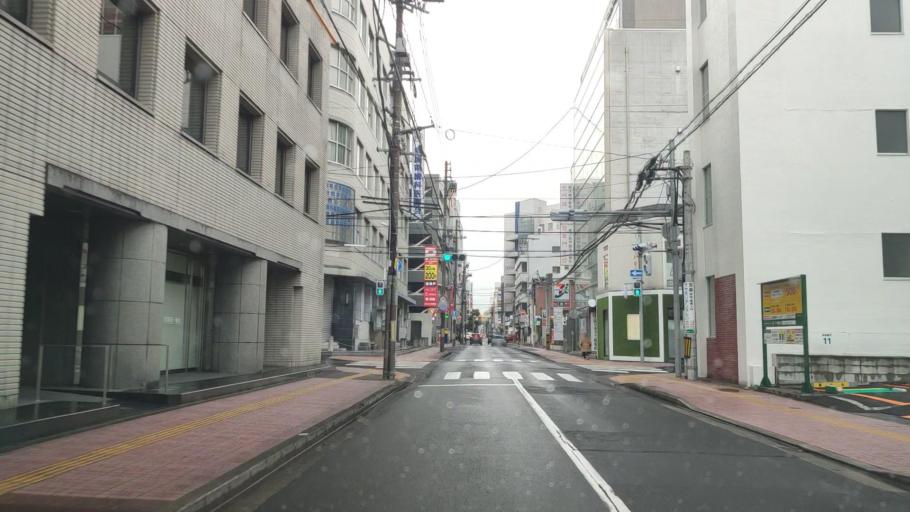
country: JP
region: Miyagi
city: Sendai
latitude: 38.2608
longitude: 140.8706
